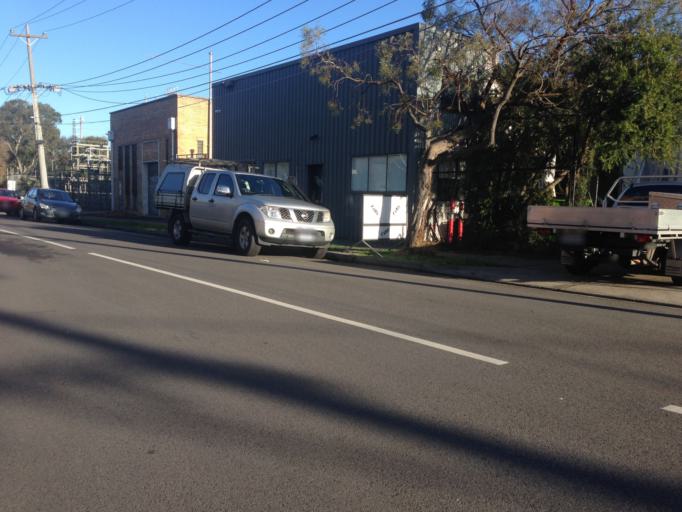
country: AU
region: Victoria
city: Alphington
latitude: -37.7784
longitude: 145.0326
